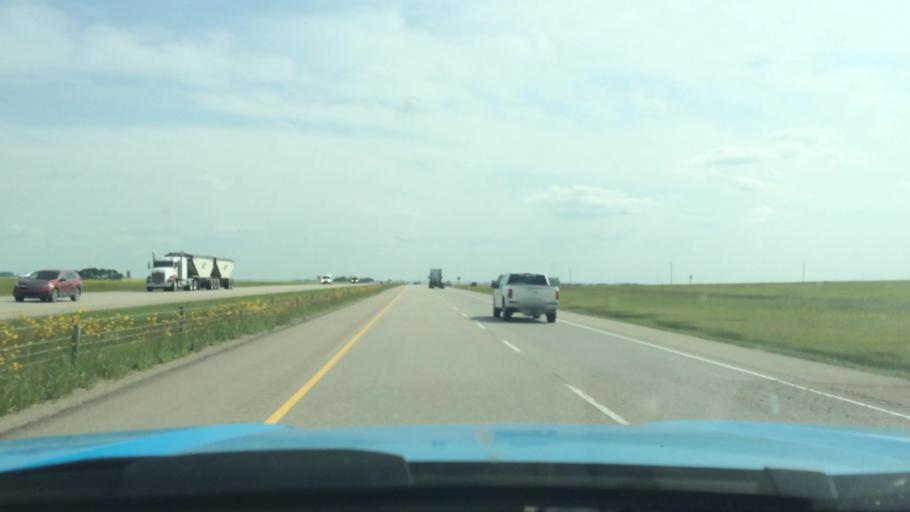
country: CA
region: Alberta
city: Didsbury
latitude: 51.6634
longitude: -114.0256
